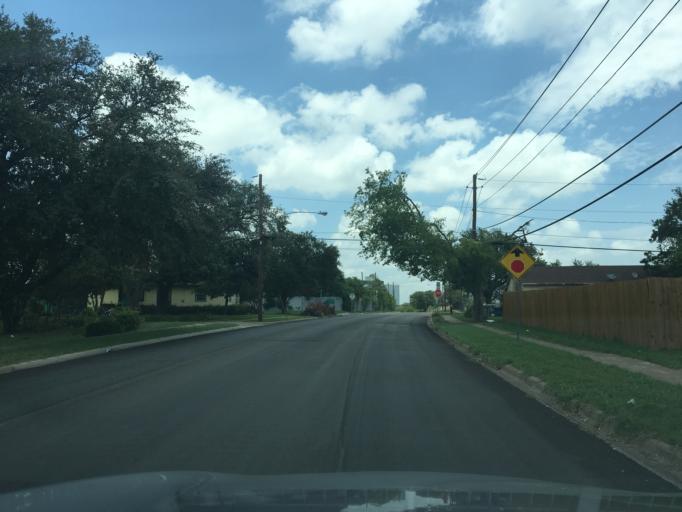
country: US
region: Texas
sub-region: Dallas County
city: Richardson
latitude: 32.9160
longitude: -96.7622
